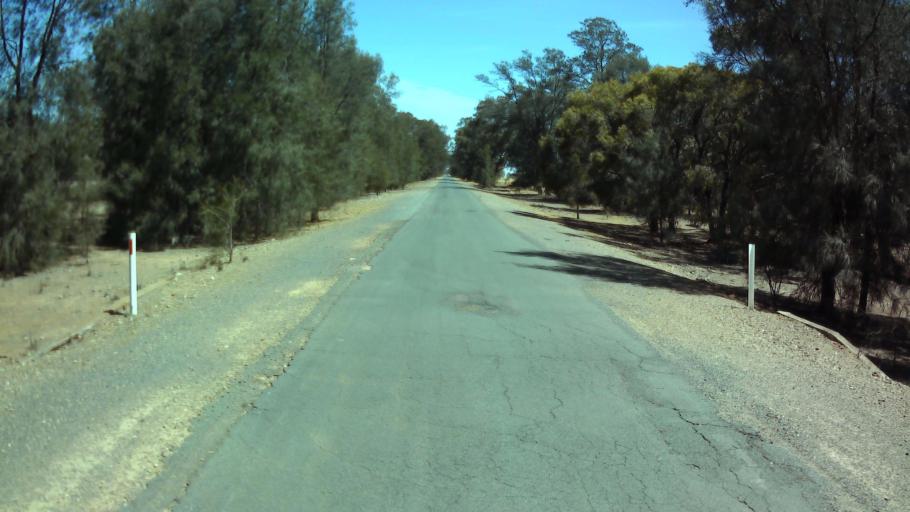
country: AU
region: New South Wales
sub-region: Weddin
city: Grenfell
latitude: -33.8785
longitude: 147.6905
